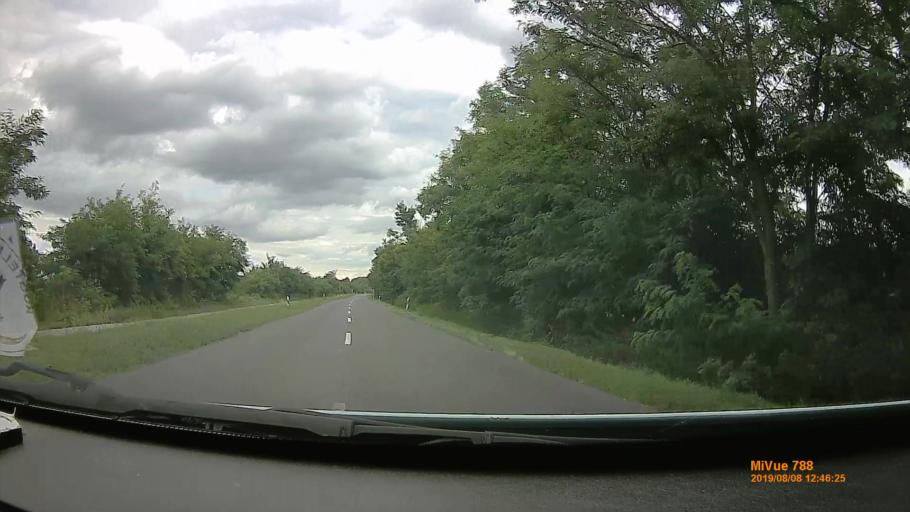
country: HU
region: Szabolcs-Szatmar-Bereg
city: Hodasz
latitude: 47.8962
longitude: 22.2192
